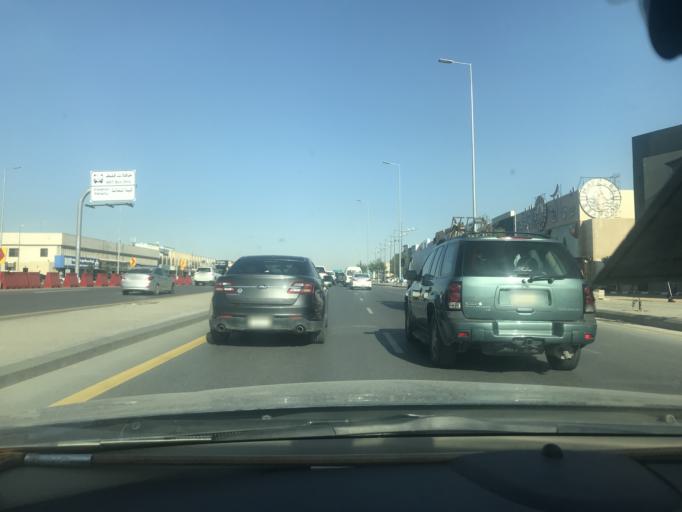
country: SA
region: Ar Riyad
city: Riyadh
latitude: 24.7249
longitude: 46.6914
